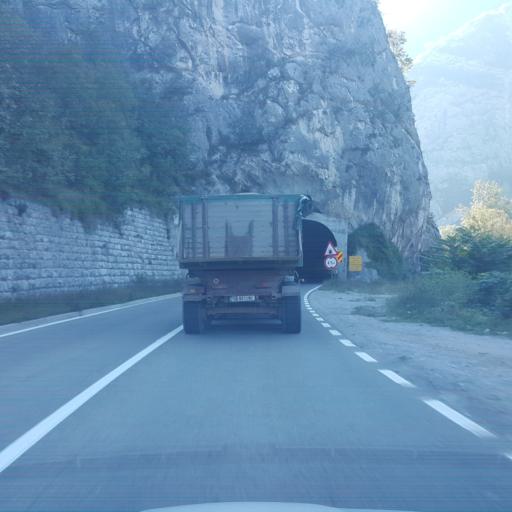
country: RS
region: Central Serbia
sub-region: Nisavski Okrug
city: Svrljig
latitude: 43.3357
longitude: 22.1332
